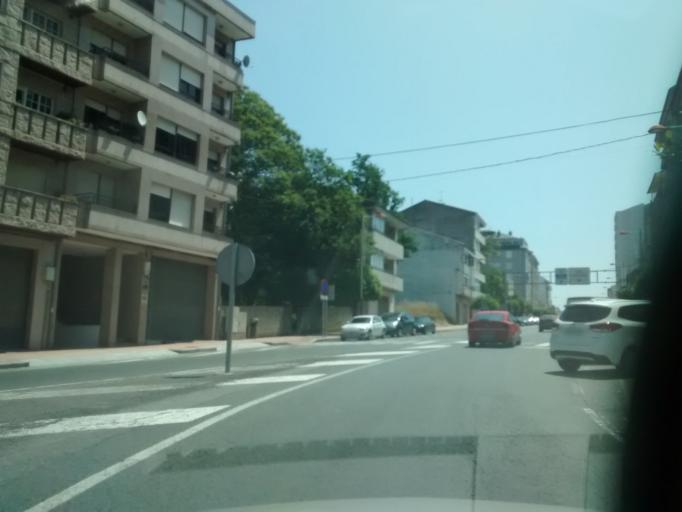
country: ES
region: Galicia
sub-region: Provincia de Ourense
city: O Carballino
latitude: 42.4347
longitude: -8.0775
